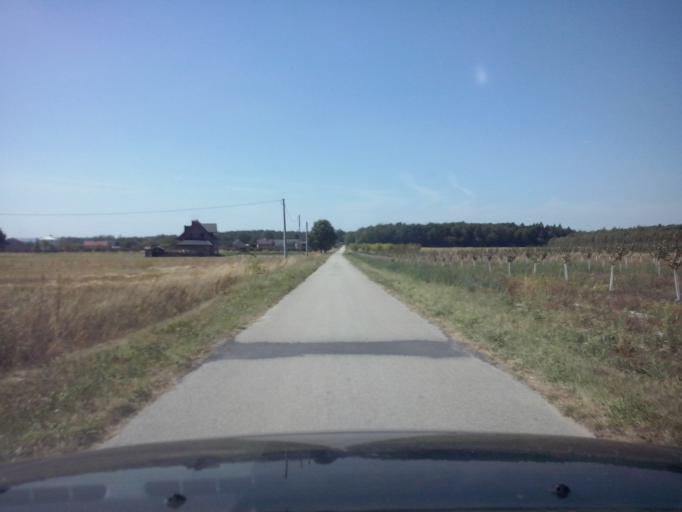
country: PL
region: Swietokrzyskie
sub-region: Powiat buski
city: Gnojno
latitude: 50.6069
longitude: 20.9238
